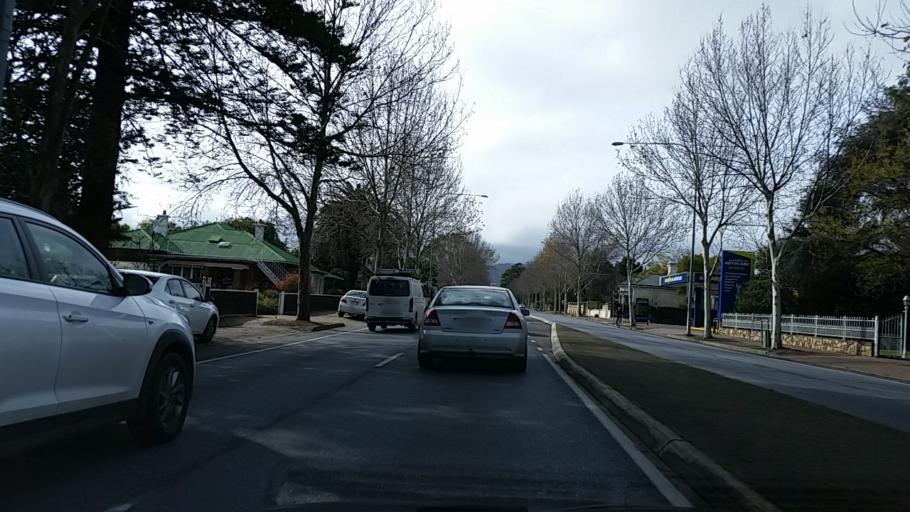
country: AU
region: South Australia
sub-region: Unley
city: Unley Park
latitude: -34.9658
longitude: 138.6015
